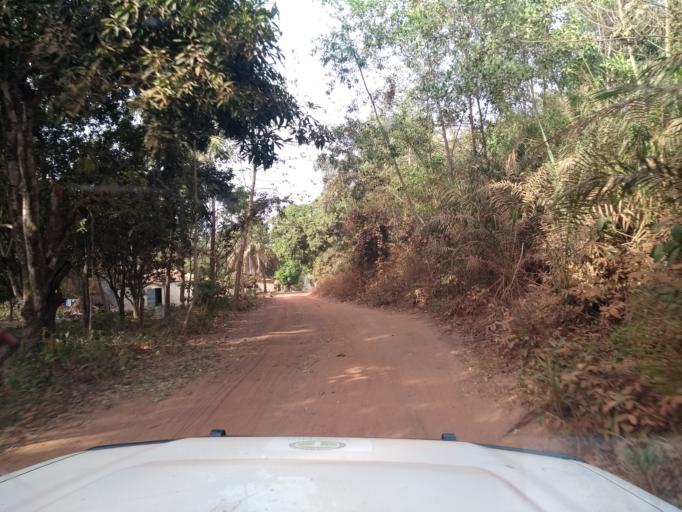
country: GN
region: Kindia
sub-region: Prefecture de Dubreka
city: Dubreka
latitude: 9.8591
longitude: -13.5474
